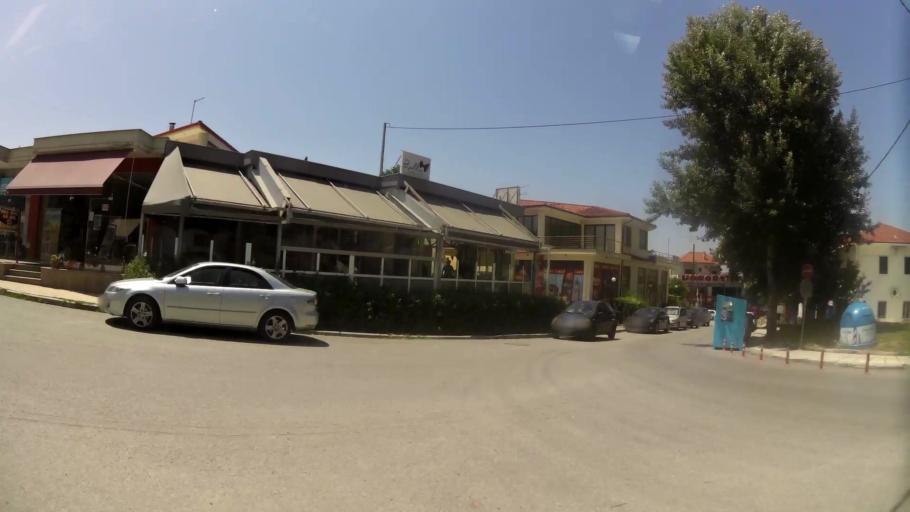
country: GR
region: Central Macedonia
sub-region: Nomos Thessalonikis
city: Trilofos
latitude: 40.4672
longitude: 22.9696
